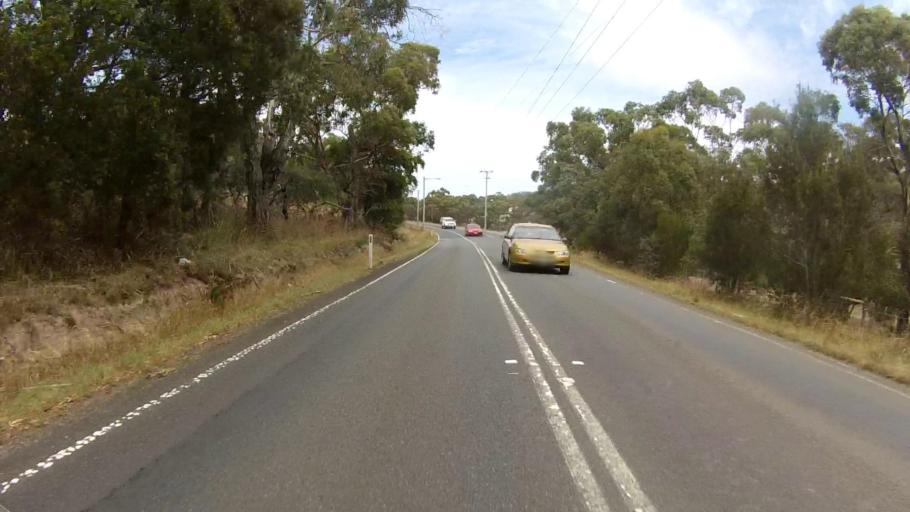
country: AU
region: Tasmania
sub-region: Clarence
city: Acton Park
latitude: -42.8725
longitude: 147.4829
